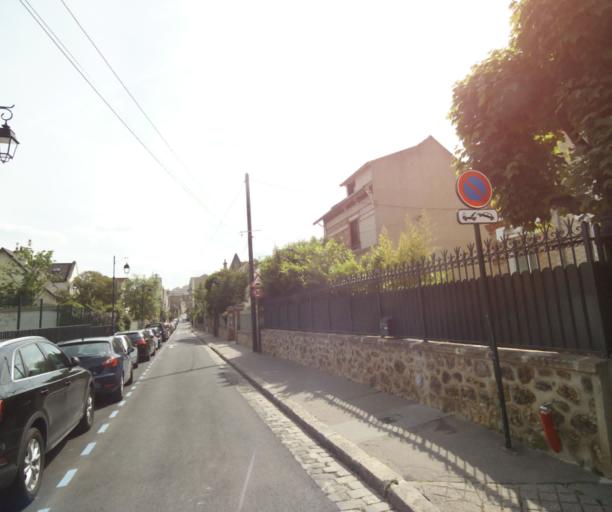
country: FR
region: Ile-de-France
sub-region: Departement des Hauts-de-Seine
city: Colombes
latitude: 48.9276
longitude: 2.2565
